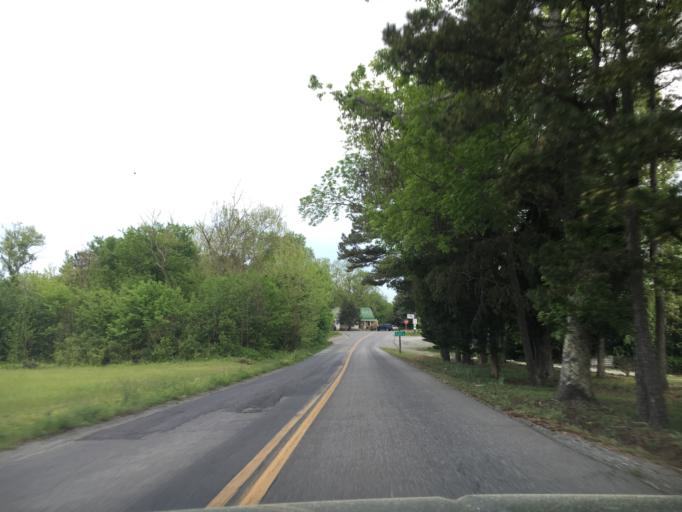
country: US
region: Virginia
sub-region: Campbell County
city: Brookneal
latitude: 36.9222
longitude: -78.9487
